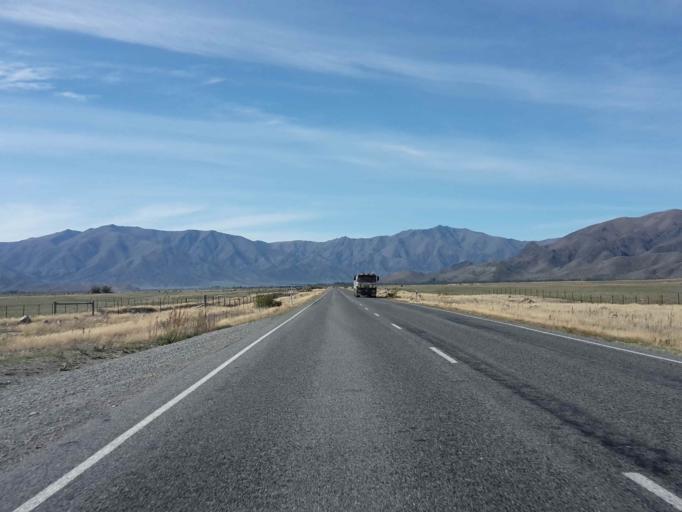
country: NZ
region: Otago
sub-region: Queenstown-Lakes District
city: Wanaka
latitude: -44.5064
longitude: 169.8691
